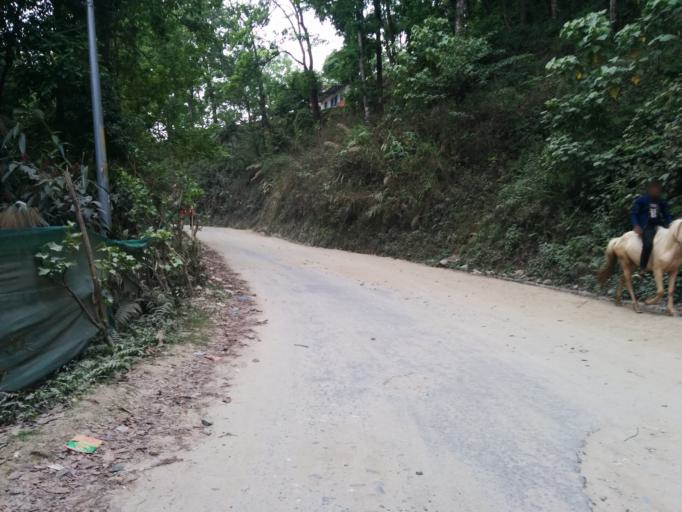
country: NP
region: Western Region
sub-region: Gandaki Zone
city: Pokhara
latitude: 28.2213
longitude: 83.9534
